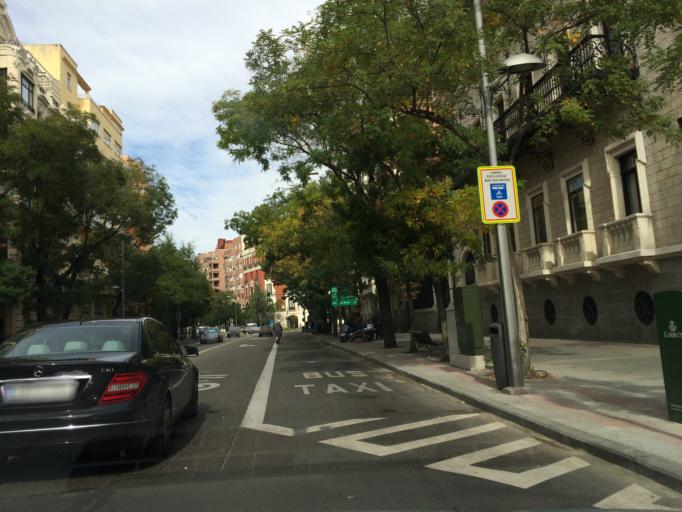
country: ES
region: Madrid
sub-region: Provincia de Madrid
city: Chamberi
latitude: 40.4318
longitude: -3.6918
